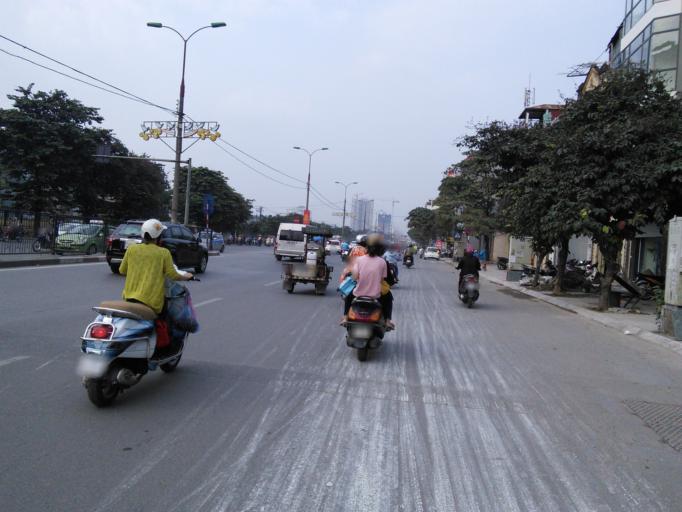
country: VN
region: Ha Noi
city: Van Dien
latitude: 20.9729
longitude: 105.8409
